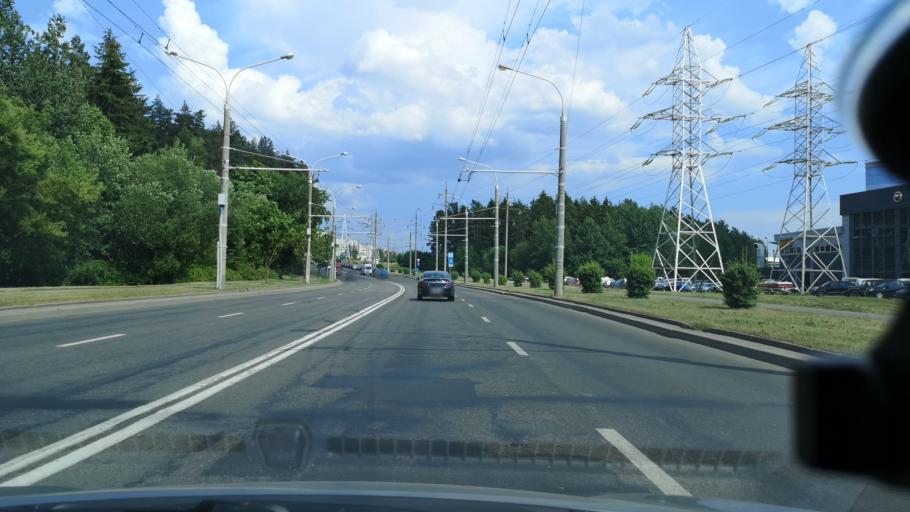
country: BY
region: Minsk
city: Borovlyany
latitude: 53.9446
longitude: 27.6592
